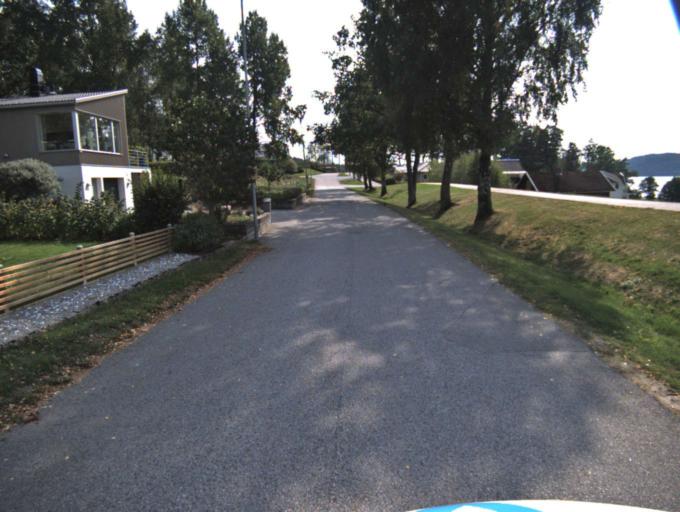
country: SE
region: Vaestra Goetaland
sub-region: Ulricehamns Kommun
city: Ulricehamn
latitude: 57.7774
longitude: 13.4053
